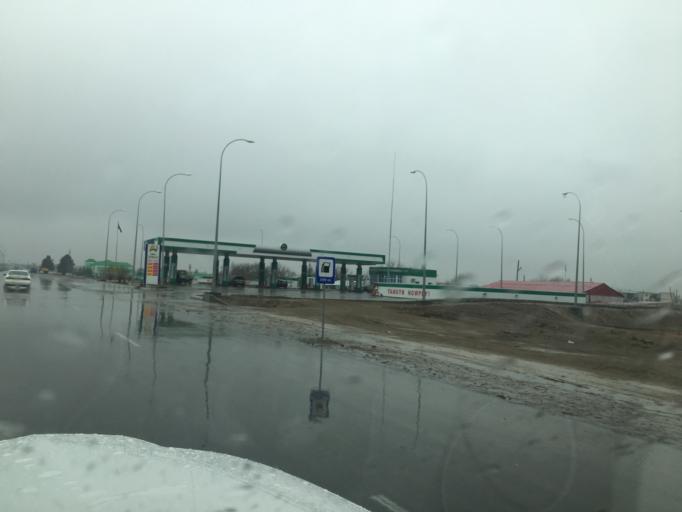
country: TM
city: Murgab
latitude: 37.5008
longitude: 61.9580
